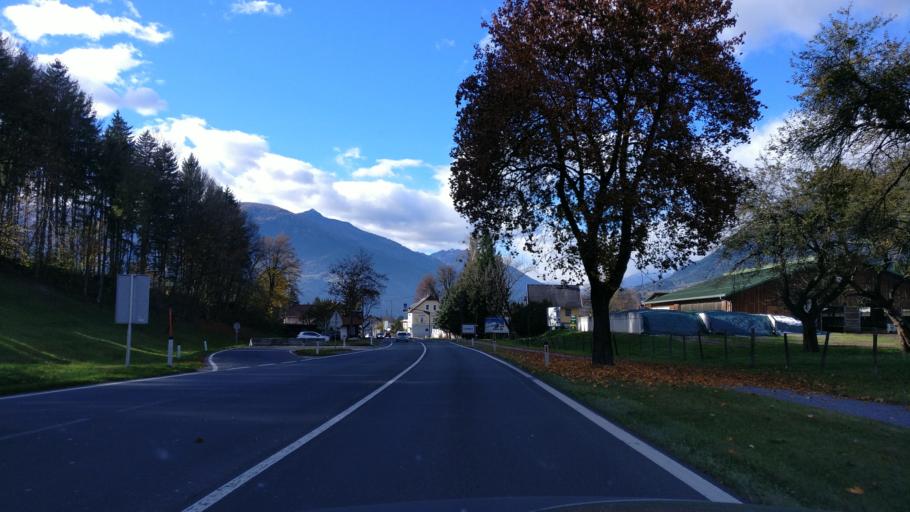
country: AT
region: Carinthia
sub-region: Politischer Bezirk Spittal an der Drau
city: Lendorf
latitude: 46.8304
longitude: 13.4268
